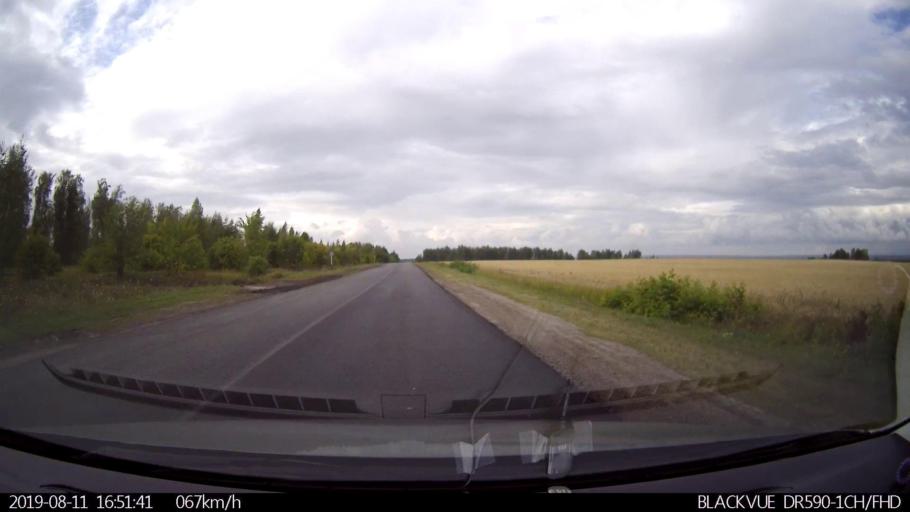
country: RU
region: Ulyanovsk
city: Mayna
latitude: 54.2397
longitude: 47.6762
